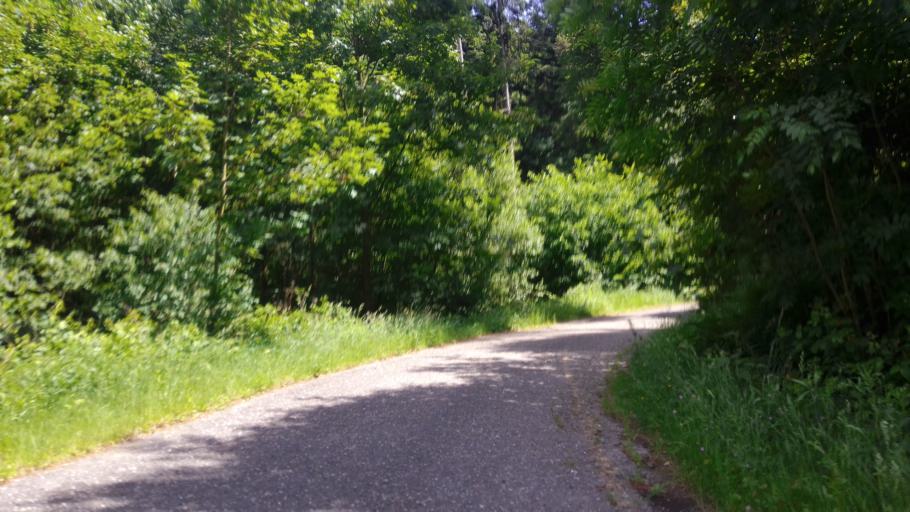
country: DE
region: Baden-Wuerttemberg
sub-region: Karlsruhe Region
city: Sinzheim
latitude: 48.7394
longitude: 8.1964
